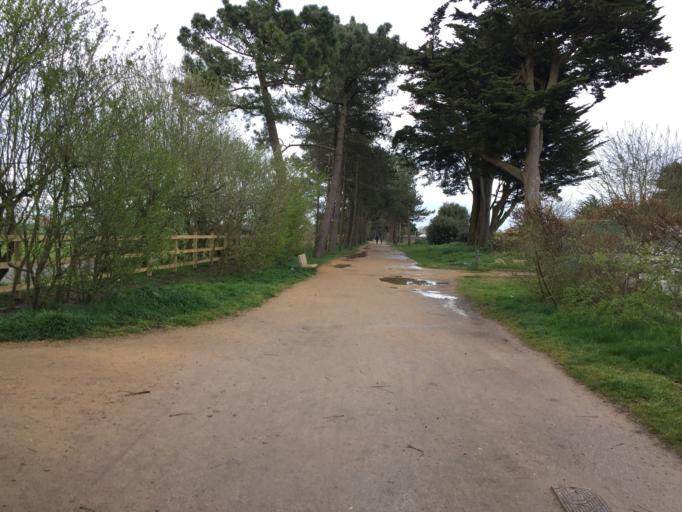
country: JE
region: St Helier
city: Saint Helier
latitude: 49.1930
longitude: -2.2068
